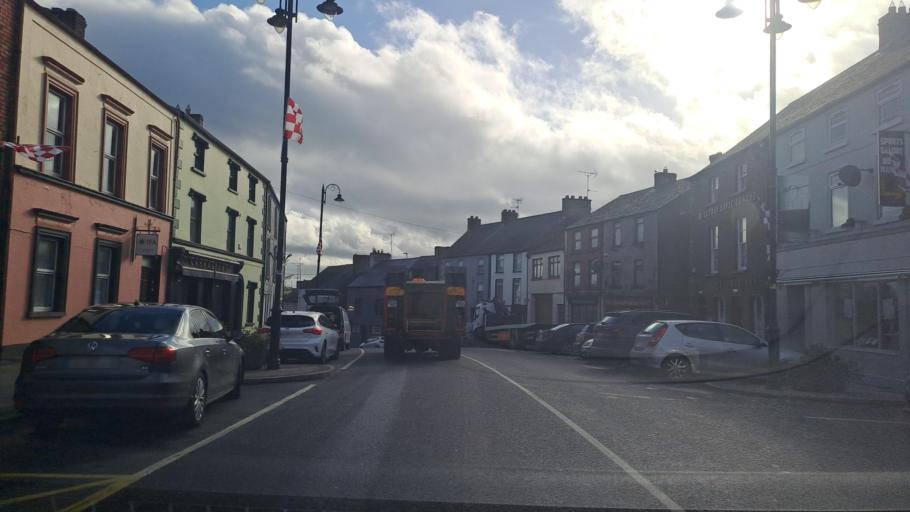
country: IE
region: Ulster
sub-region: County Monaghan
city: Monaghan
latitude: 54.1278
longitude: -6.9027
